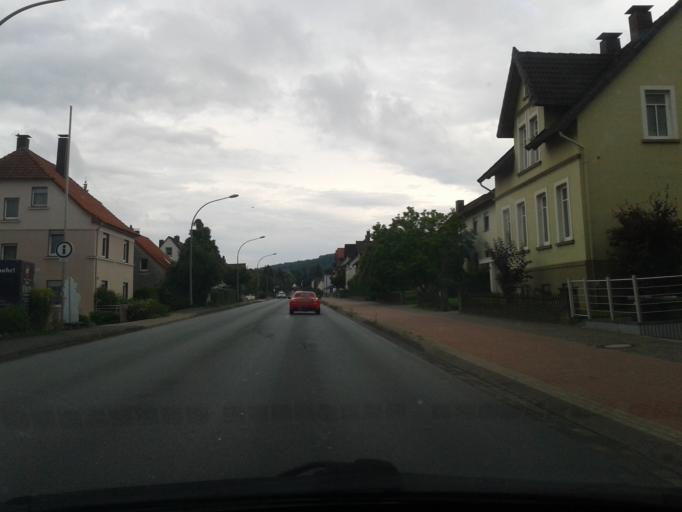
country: DE
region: North Rhine-Westphalia
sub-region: Regierungsbezirk Detmold
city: Detmold
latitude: 51.9179
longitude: 8.9035
